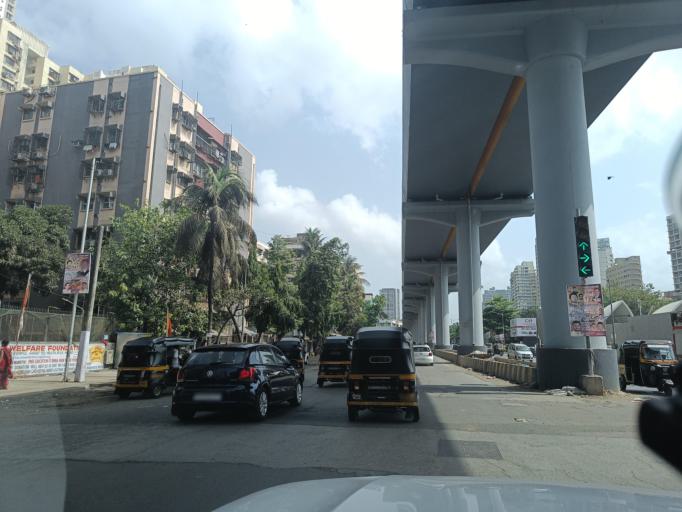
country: IN
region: Maharashtra
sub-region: Mumbai Suburban
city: Powai
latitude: 19.1416
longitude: 72.8313
